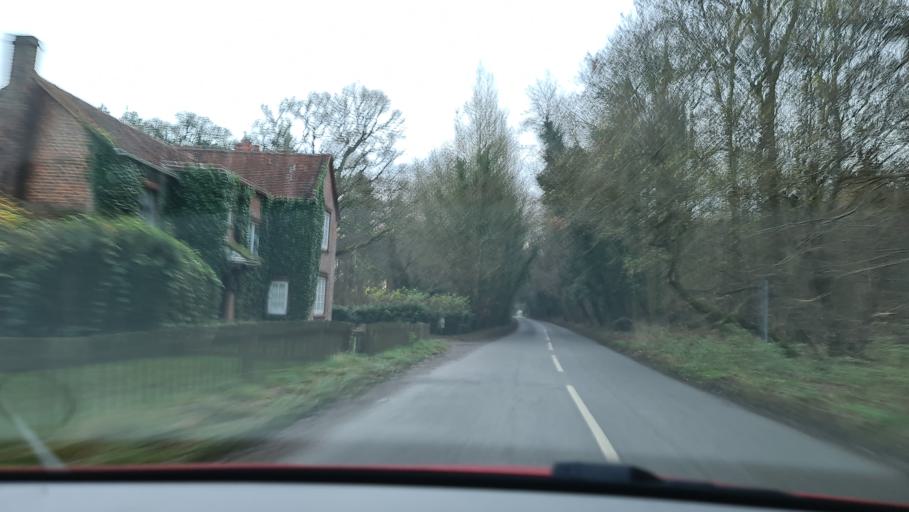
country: GB
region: England
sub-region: Buckinghamshire
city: Great Missenden
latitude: 51.7140
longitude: -0.7518
